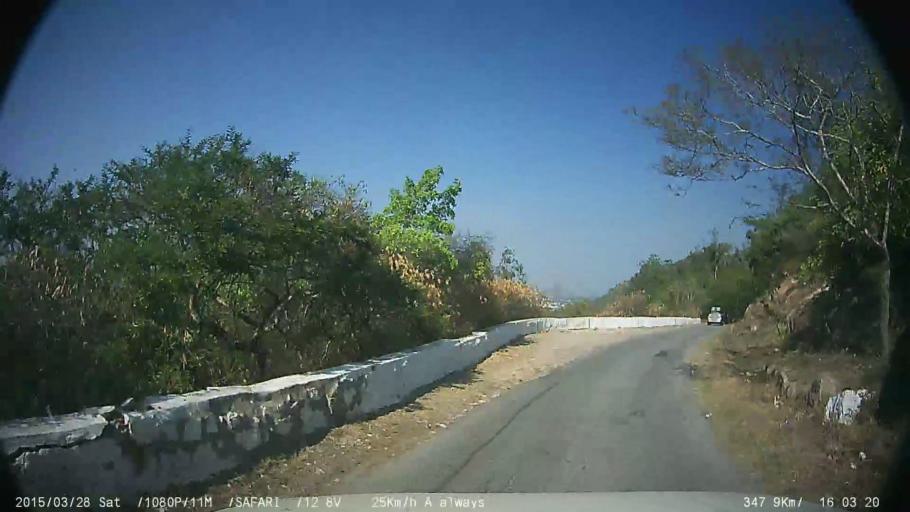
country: IN
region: Karnataka
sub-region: Mysore
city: Mysore
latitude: 12.2809
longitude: 76.6690
